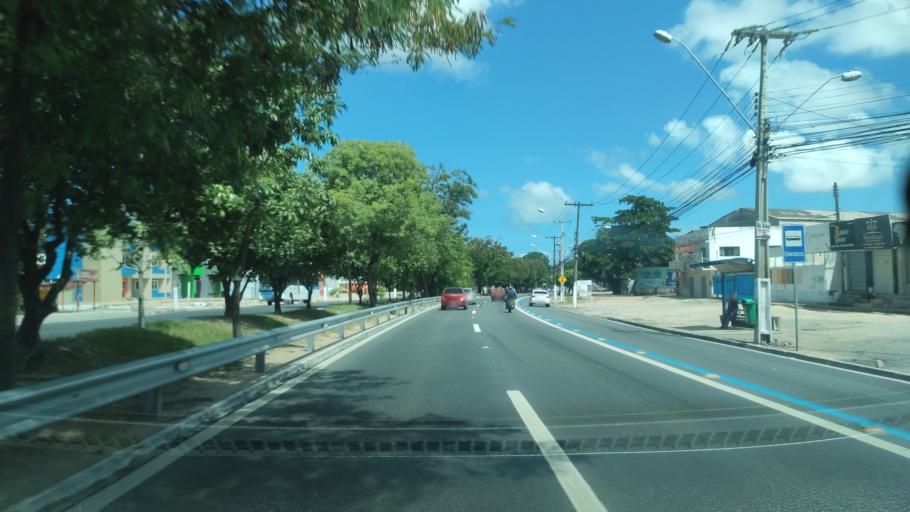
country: BR
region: Alagoas
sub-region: Maceio
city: Maceio
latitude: -9.6076
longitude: -35.7407
